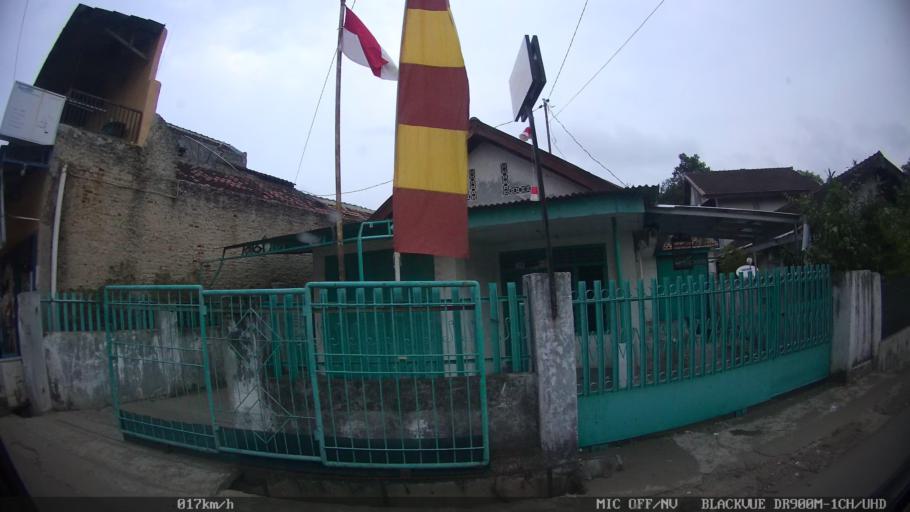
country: ID
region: Lampung
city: Kedaton
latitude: -5.4045
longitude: 105.2670
